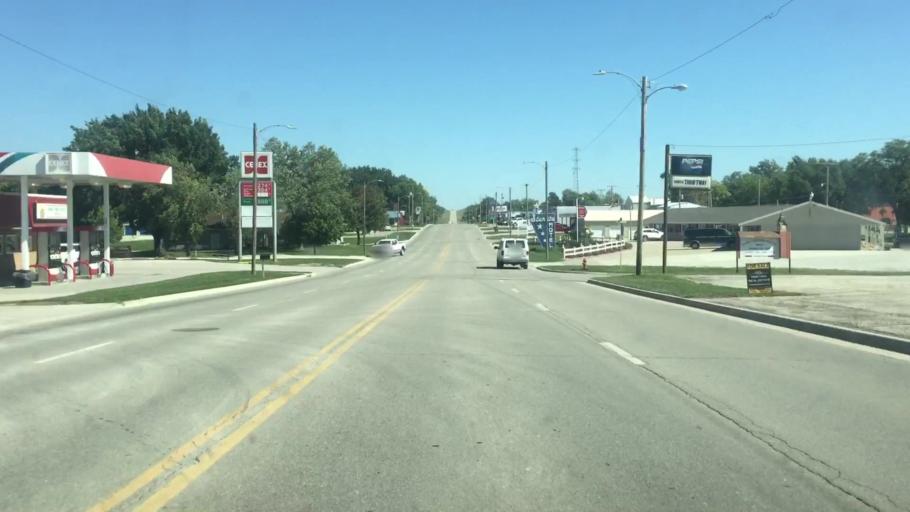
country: US
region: Kansas
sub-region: Nemaha County
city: Seneca
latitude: 39.8413
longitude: -96.0633
